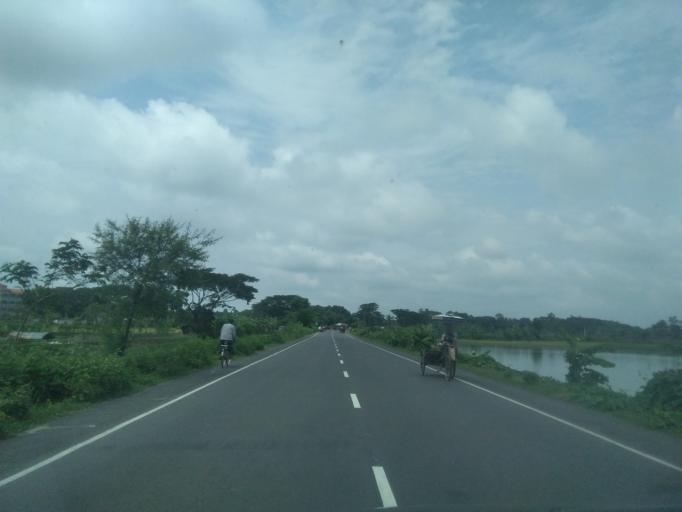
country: BD
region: Khulna
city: Kesabpur
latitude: 22.8088
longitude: 89.2416
